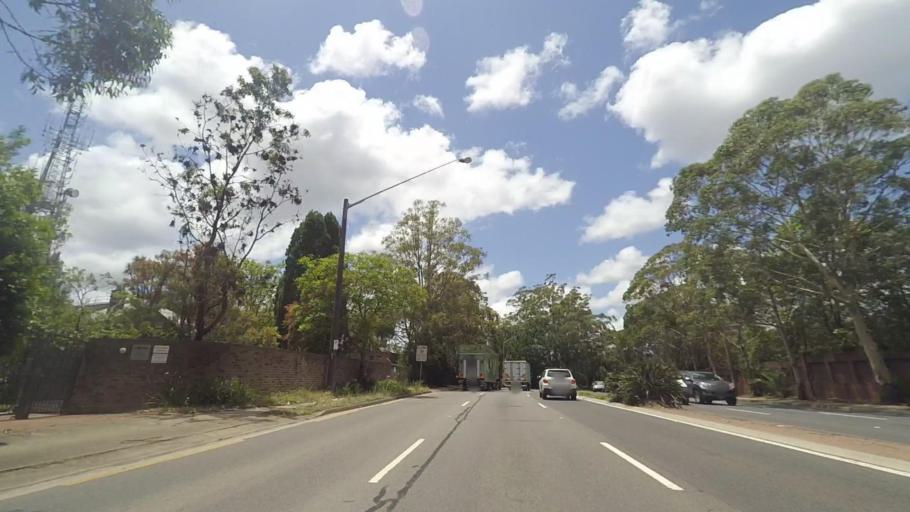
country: AU
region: New South Wales
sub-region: Hornsby Shire
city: Beecroft
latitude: -33.7409
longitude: 151.0577
